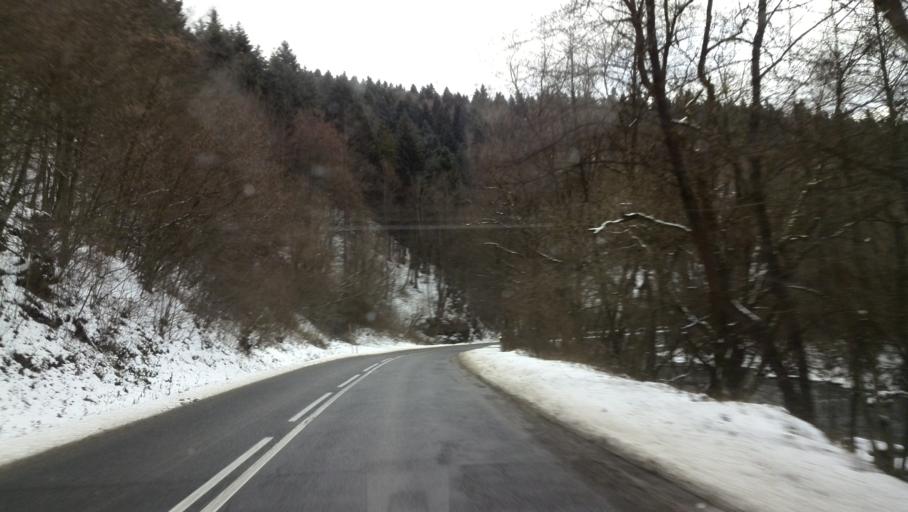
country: SK
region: Kosicky
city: Gelnica
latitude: 48.8679
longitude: 20.9760
